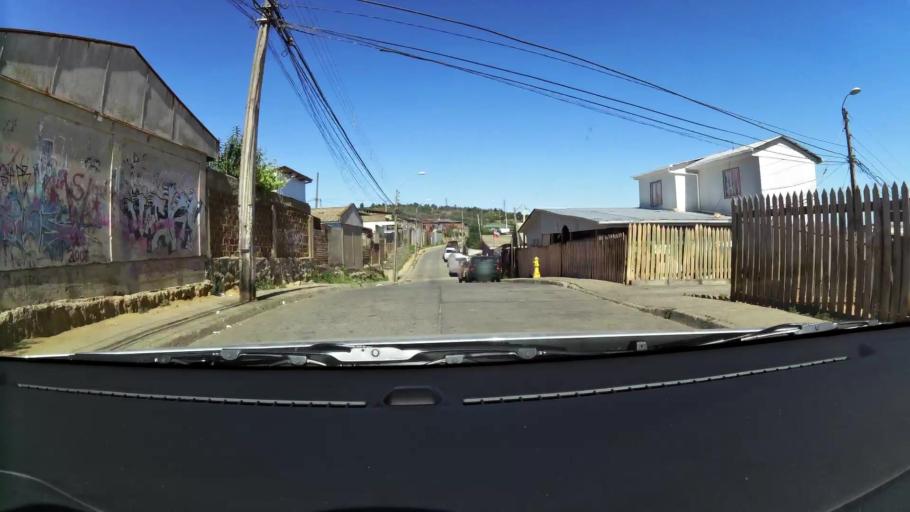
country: CL
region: Valparaiso
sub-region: Provincia de Valparaiso
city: Valparaiso
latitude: -33.0725
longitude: -71.5829
